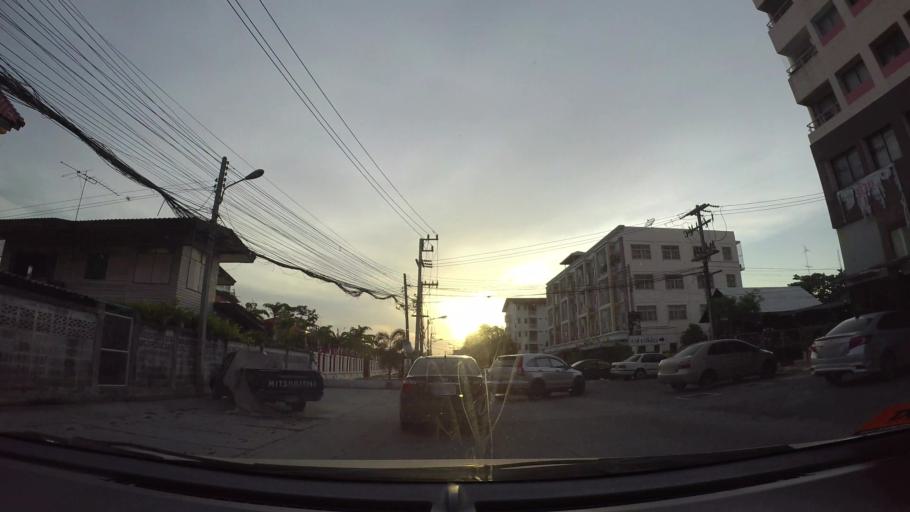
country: TH
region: Chon Buri
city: Chon Buri
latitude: 13.3558
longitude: 100.9822
